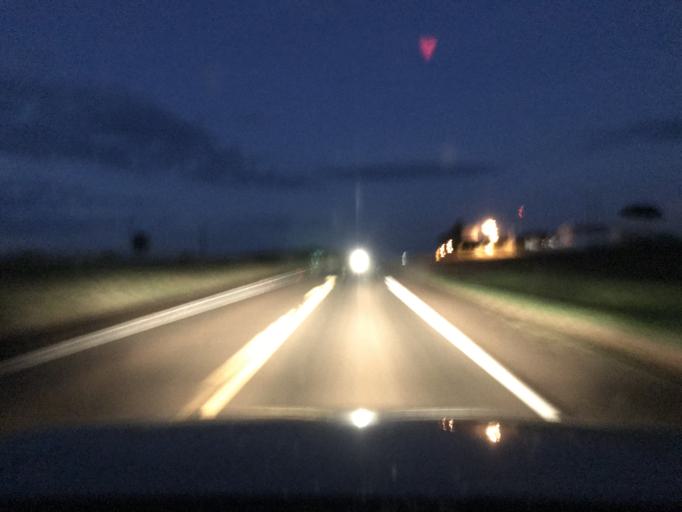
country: PY
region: Canindeyu
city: Salto del Guaira
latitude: -24.1026
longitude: -54.2309
